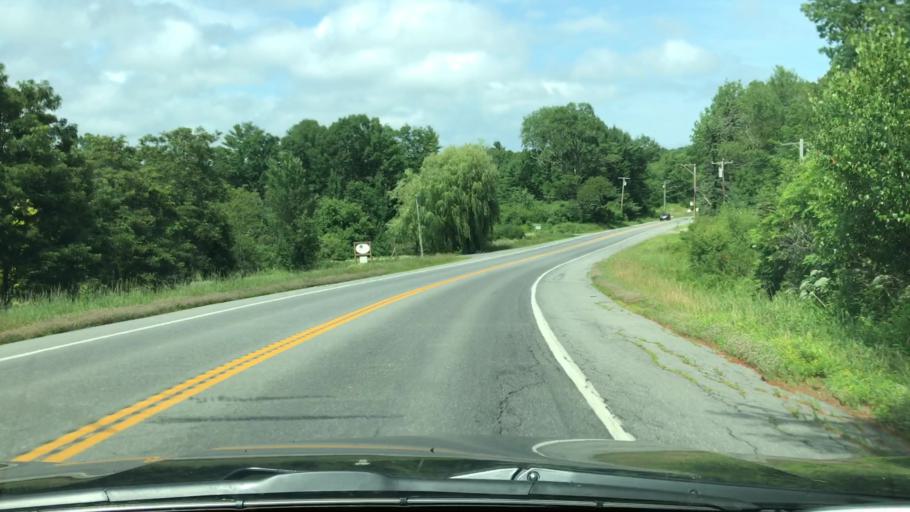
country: US
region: Maine
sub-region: Waldo County
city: Belfast
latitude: 44.3917
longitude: -68.9908
